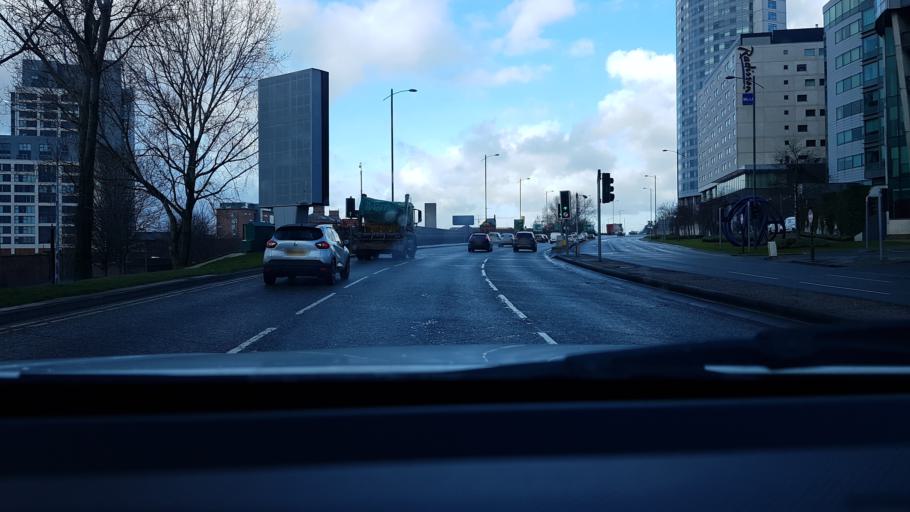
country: GB
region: England
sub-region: Liverpool
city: Liverpool
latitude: 53.4093
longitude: -2.9973
